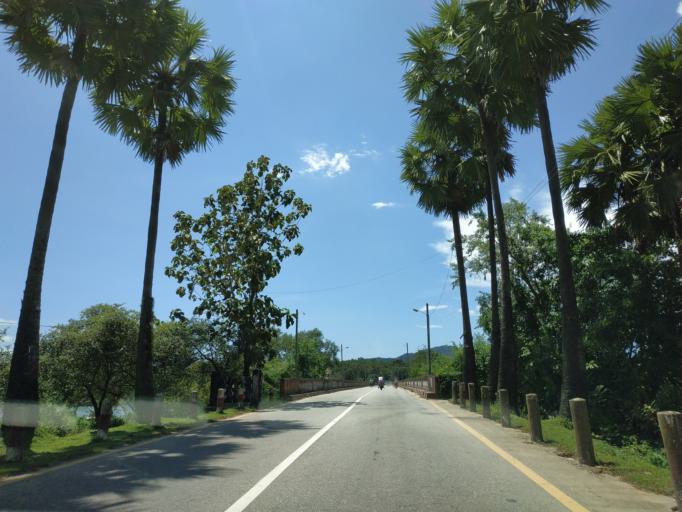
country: MM
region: Tanintharyi
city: Dawei
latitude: 14.0946
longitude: 98.1762
